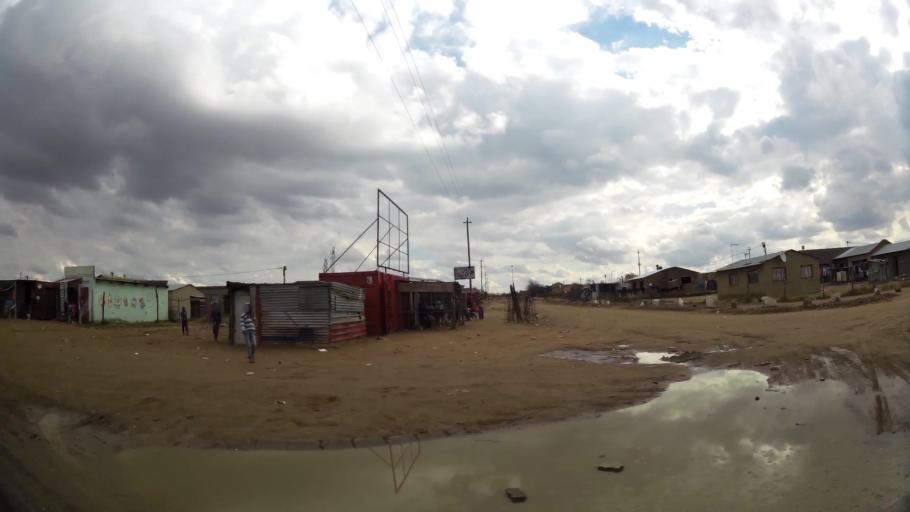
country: ZA
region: Orange Free State
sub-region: Fezile Dabi District Municipality
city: Sasolburg
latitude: -26.8752
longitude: 27.8733
